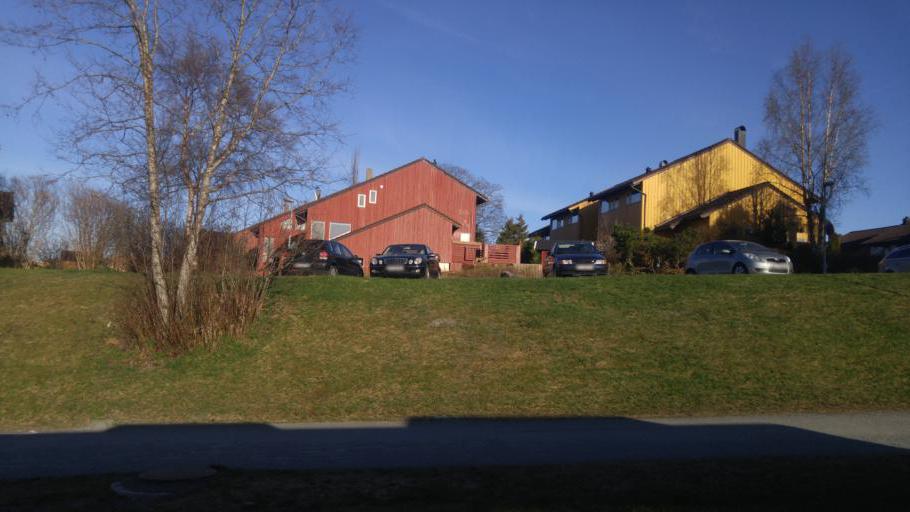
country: NO
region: Sor-Trondelag
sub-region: Trondheim
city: Trondheim
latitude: 63.4174
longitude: 10.4474
